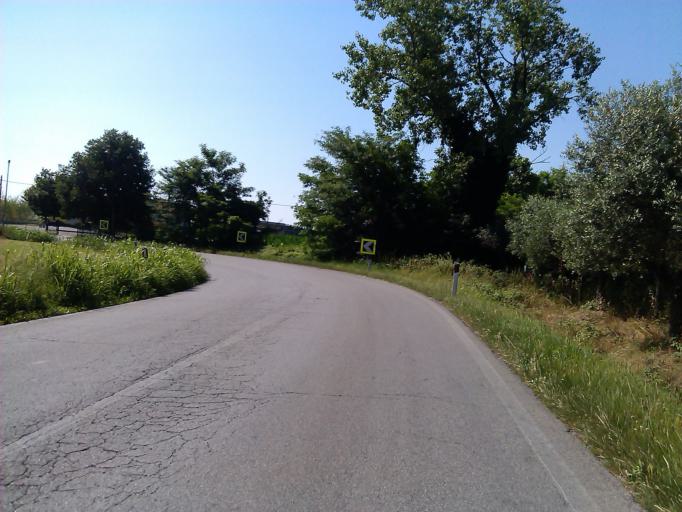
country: IT
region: Veneto
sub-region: Provincia di Vicenza
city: Cassola
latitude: 45.7350
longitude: 11.8208
